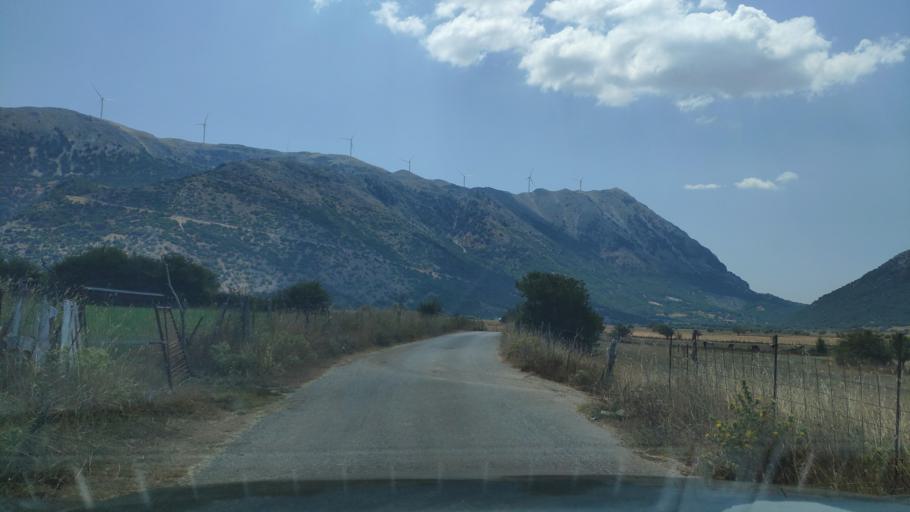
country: GR
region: West Greece
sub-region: Nomos Aitolias kai Akarnanias
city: Monastirakion
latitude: 38.7899
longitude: 20.9627
